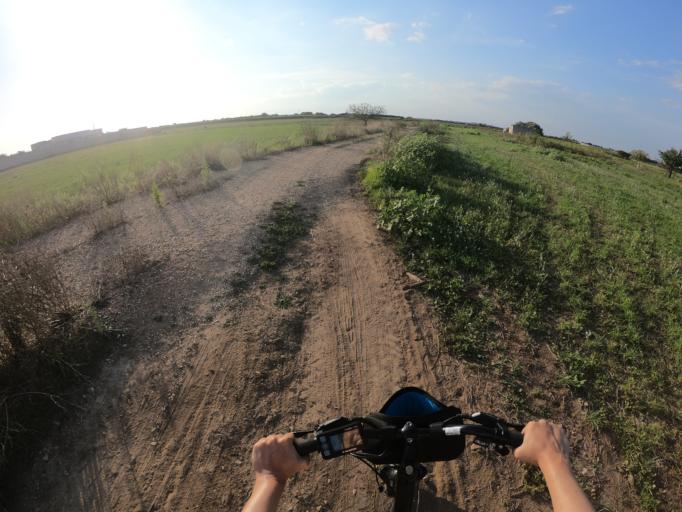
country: IT
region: Apulia
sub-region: Provincia di Lecce
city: Nardo
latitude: 40.1695
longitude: 18.0127
